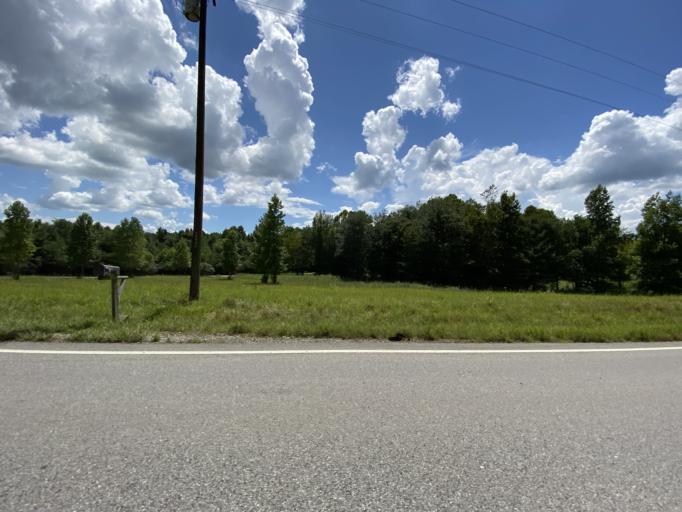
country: US
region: Alabama
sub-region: Lauderdale County
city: Underwood-Petersville
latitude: 34.9631
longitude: -87.8836
